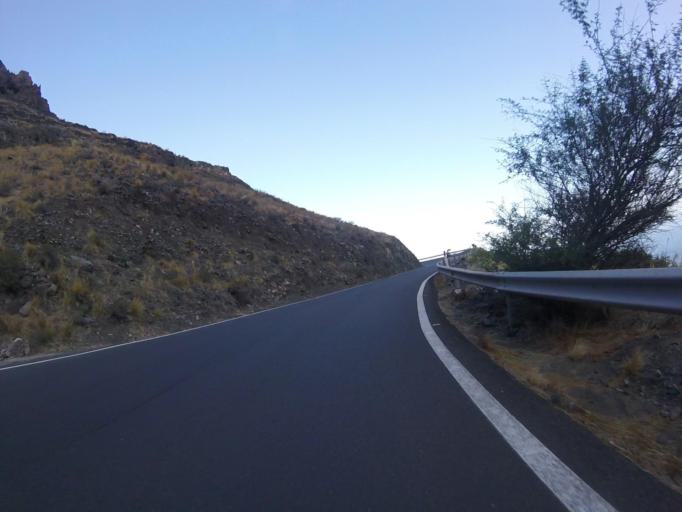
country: ES
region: Canary Islands
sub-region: Provincia de Las Palmas
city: Agaete
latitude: 28.0701
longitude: -15.7182
